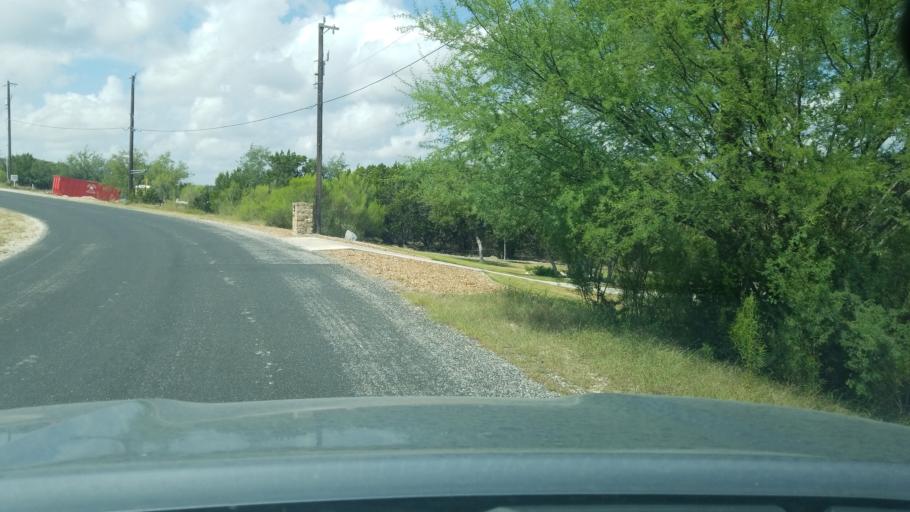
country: US
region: Texas
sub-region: Bexar County
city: Timberwood Park
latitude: 29.6793
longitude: -98.5207
